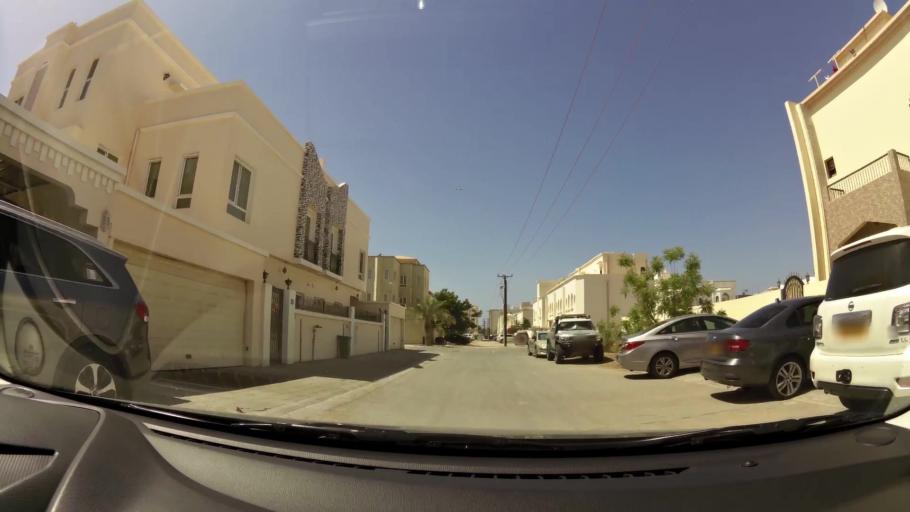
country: OM
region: Muhafazat Masqat
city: Bawshar
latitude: 23.5979
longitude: 58.3580
